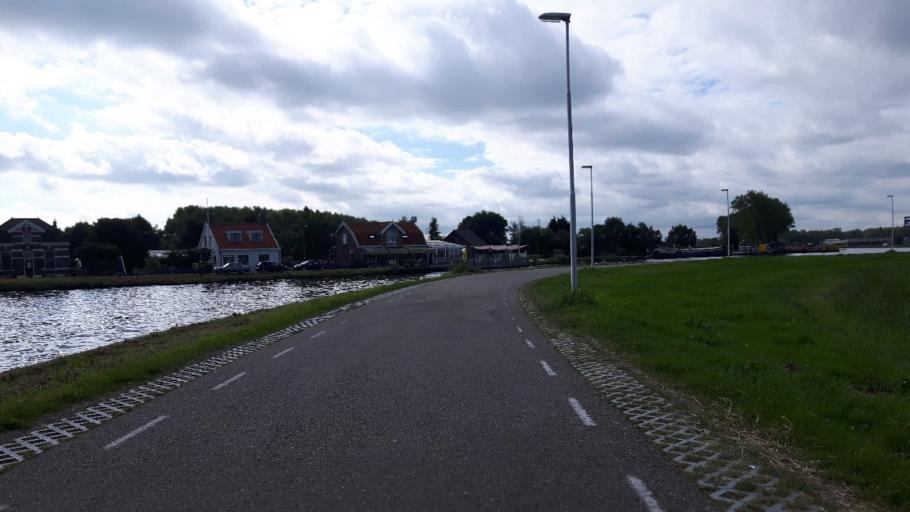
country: NL
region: North Holland
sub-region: Gemeente Landsmeer
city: Landsmeer
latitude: 52.4236
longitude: 4.9504
